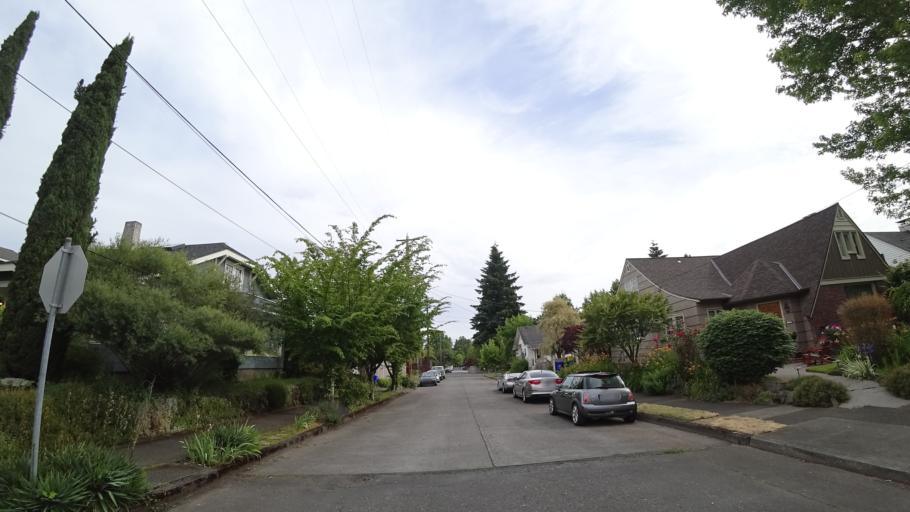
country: US
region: Oregon
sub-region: Multnomah County
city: Portland
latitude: 45.5619
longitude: -122.6926
